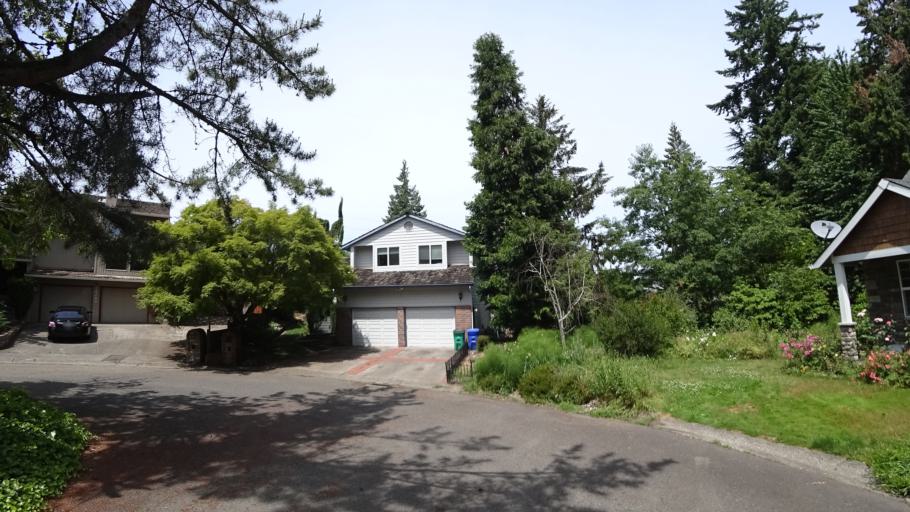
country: US
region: Oregon
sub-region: Multnomah County
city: Fairview
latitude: 45.5445
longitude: -122.4950
